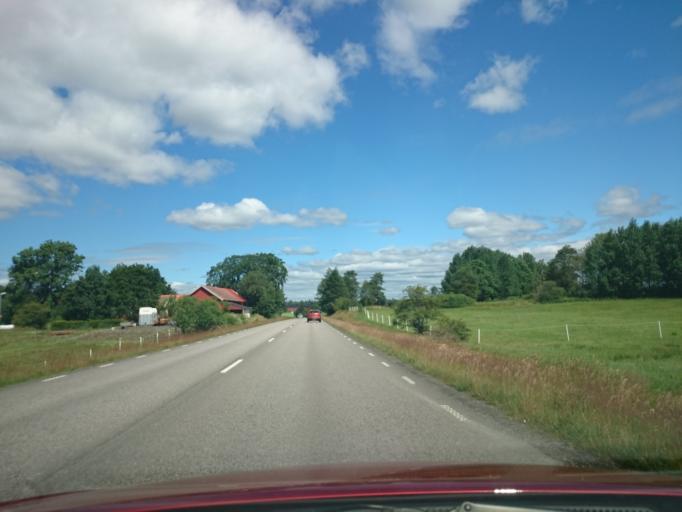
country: SE
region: Vaestra Goetaland
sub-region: Lerums Kommun
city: Stenkullen
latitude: 57.8126
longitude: 12.3017
